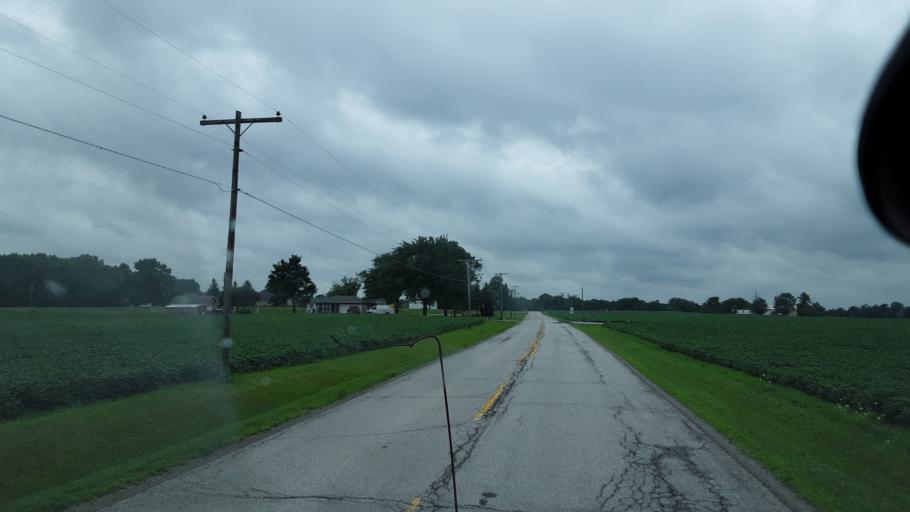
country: US
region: Indiana
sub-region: Wells County
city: Ossian
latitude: 40.9420
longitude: -85.0729
